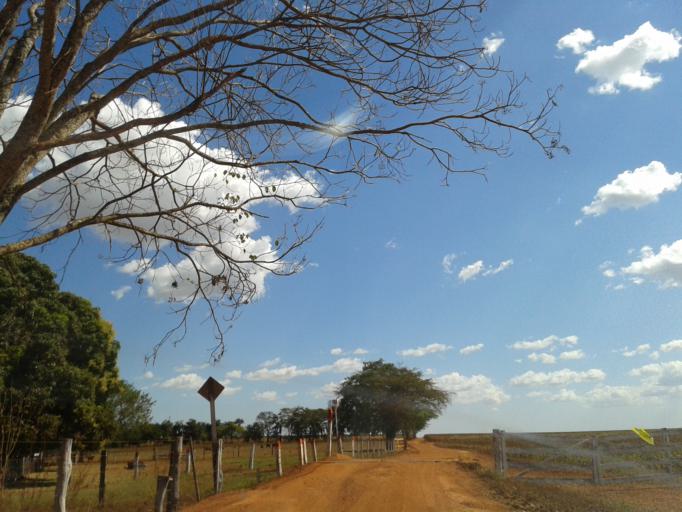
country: BR
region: Minas Gerais
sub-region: Capinopolis
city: Capinopolis
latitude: -18.6018
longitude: -49.5061
